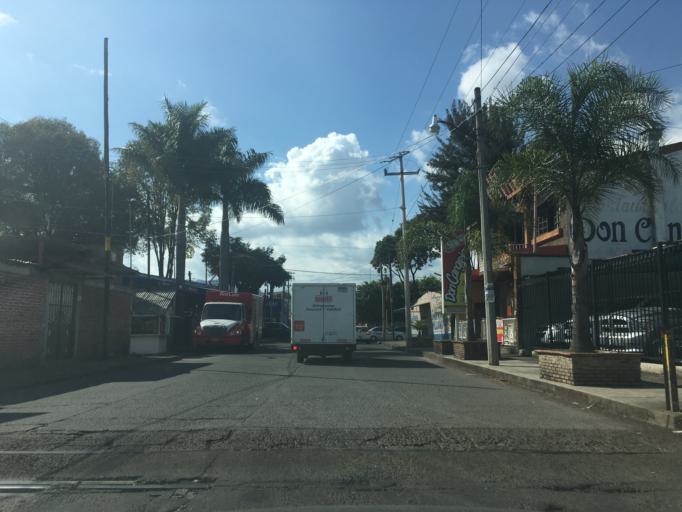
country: MX
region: Michoacan
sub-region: Uruapan
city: Uruapan
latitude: 19.4091
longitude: -102.0526
